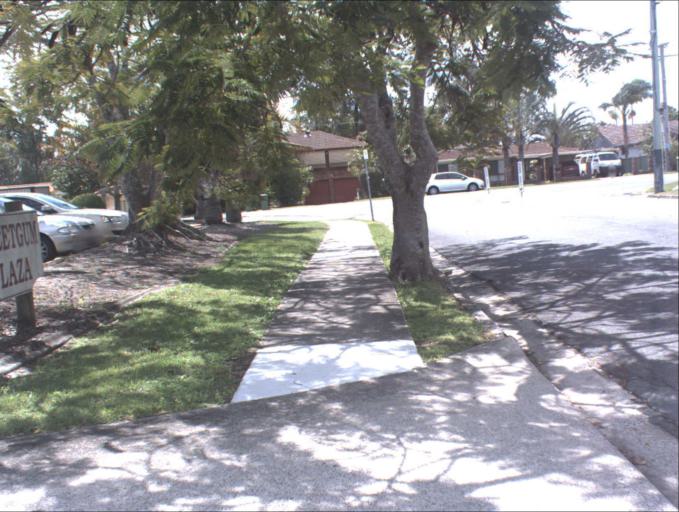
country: AU
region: Queensland
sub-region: Brisbane
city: Sunnybank Hills
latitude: -27.6645
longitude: 153.0271
